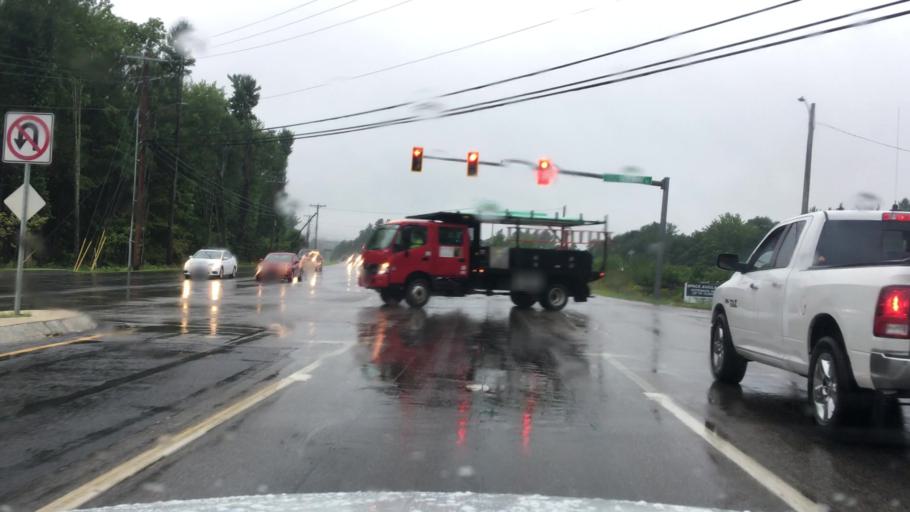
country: US
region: New Hampshire
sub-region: Strafford County
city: Rochester
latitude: 43.3341
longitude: -71.0085
